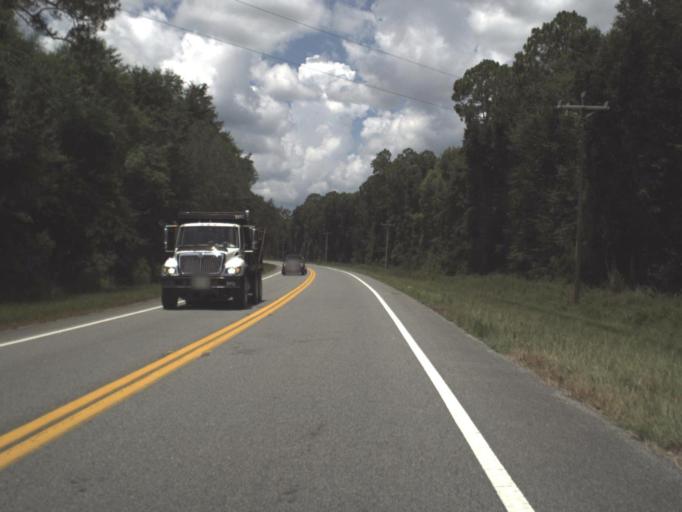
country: US
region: Florida
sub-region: Taylor County
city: Perry
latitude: 30.1421
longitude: -83.7731
